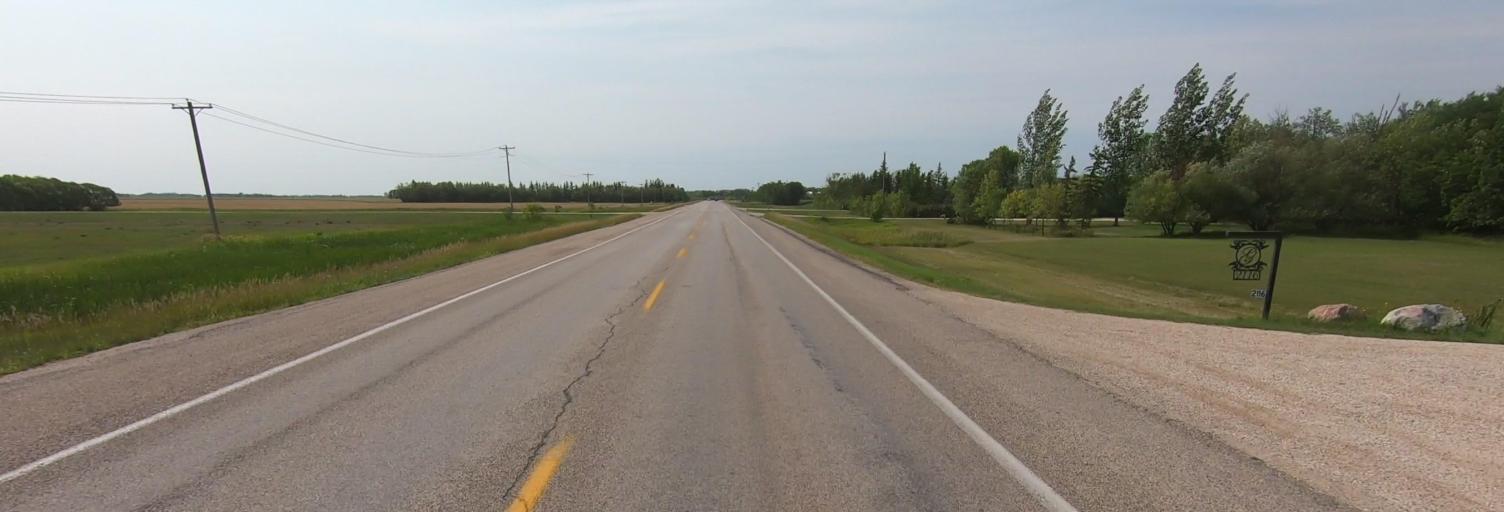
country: CA
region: Manitoba
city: Niverville
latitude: 49.6417
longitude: -97.1053
